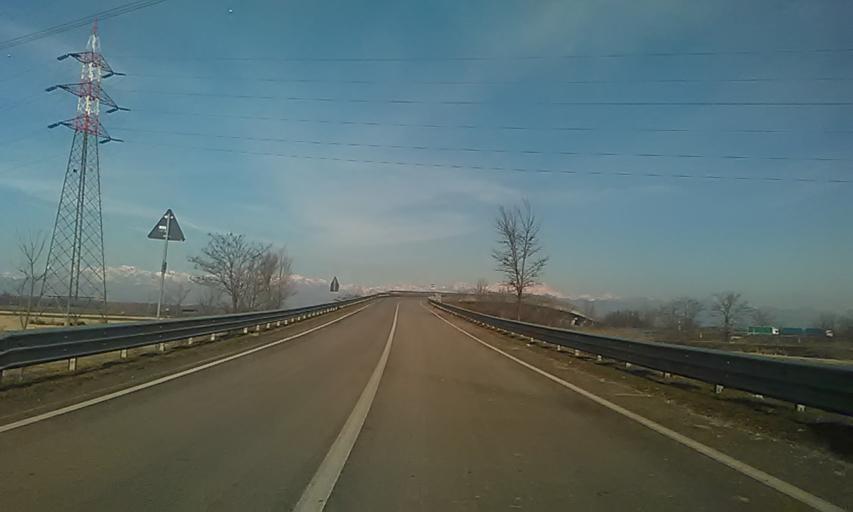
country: IT
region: Piedmont
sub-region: Provincia di Vercelli
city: Balocco
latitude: 45.4443
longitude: 8.2881
